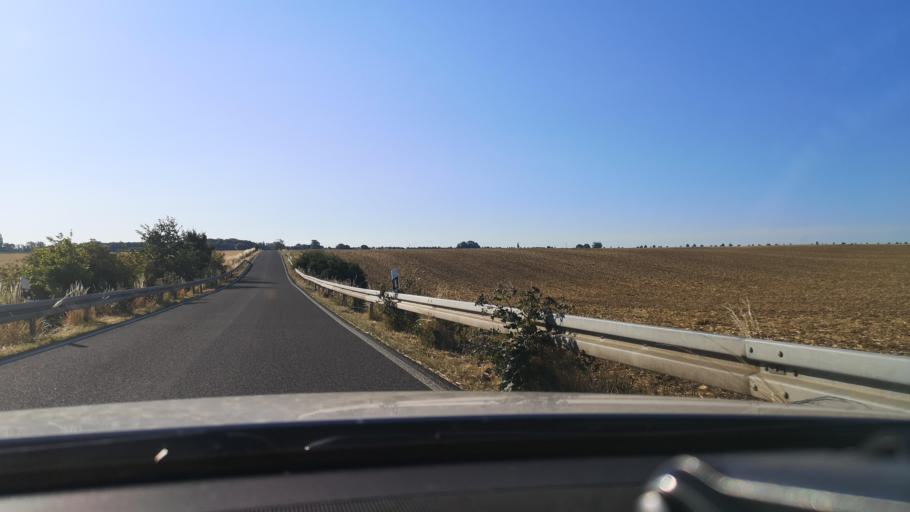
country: DE
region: Thuringia
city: Lehesten
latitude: 51.0223
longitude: 11.5756
